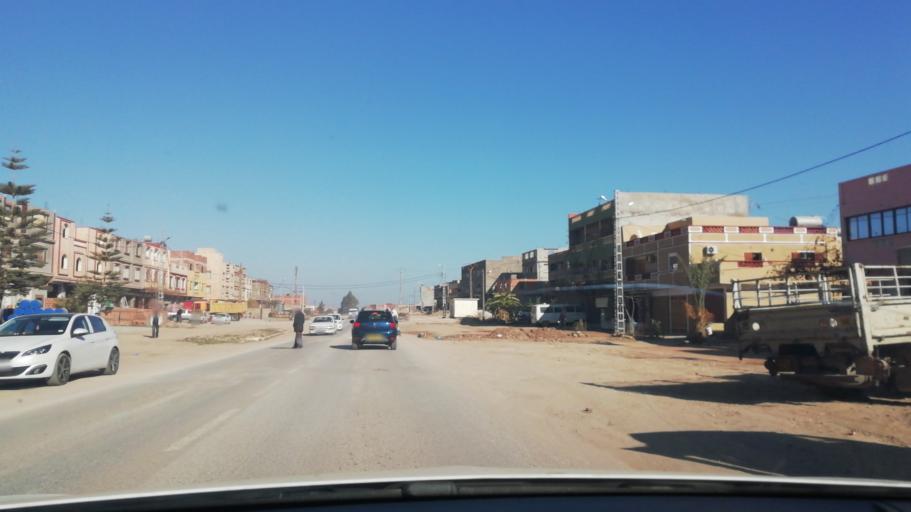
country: DZ
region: Tlemcen
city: Nedroma
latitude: 35.0089
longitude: -1.9001
